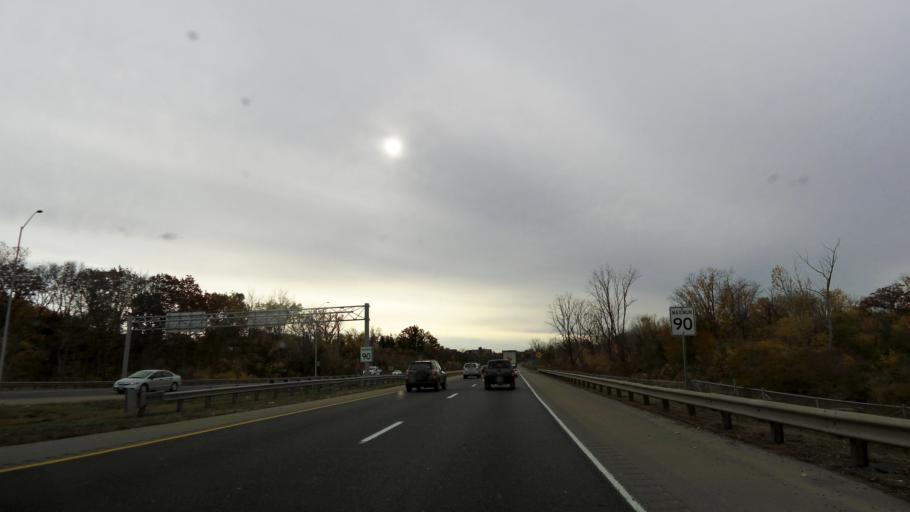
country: CA
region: Ontario
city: Hamilton
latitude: 43.2383
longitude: -79.7748
